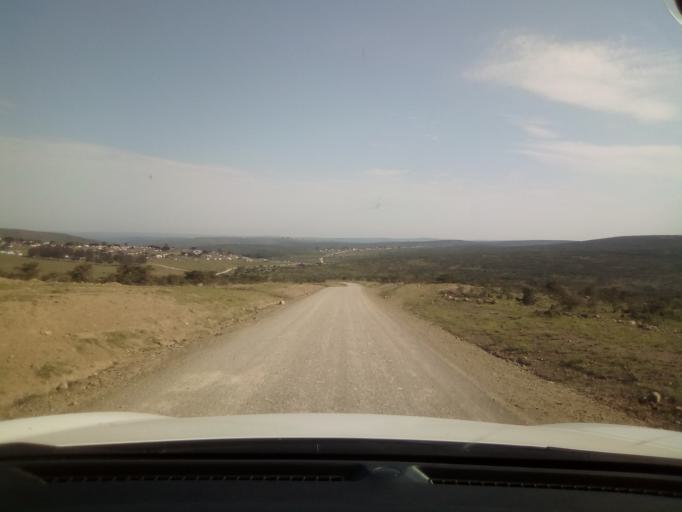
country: ZA
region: Eastern Cape
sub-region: Buffalo City Metropolitan Municipality
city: Bhisho
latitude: -32.9872
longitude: 27.2509
